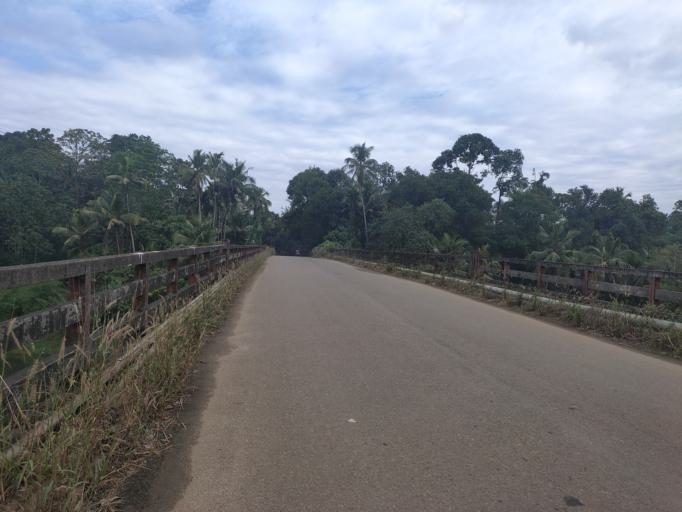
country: IN
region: Kerala
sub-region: Ernakulam
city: Muvattupula
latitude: 9.9896
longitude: 76.6365
